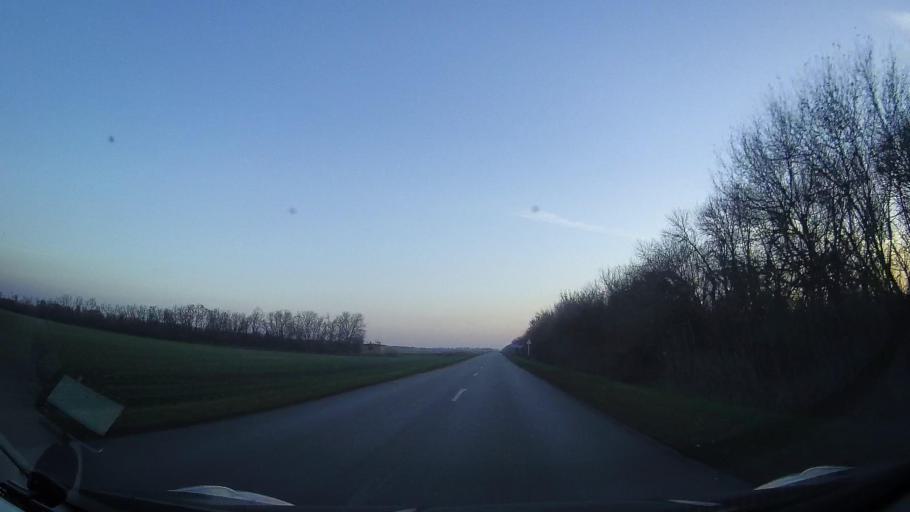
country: RU
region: Rostov
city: Zernograd
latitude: 47.0306
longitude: 40.3917
